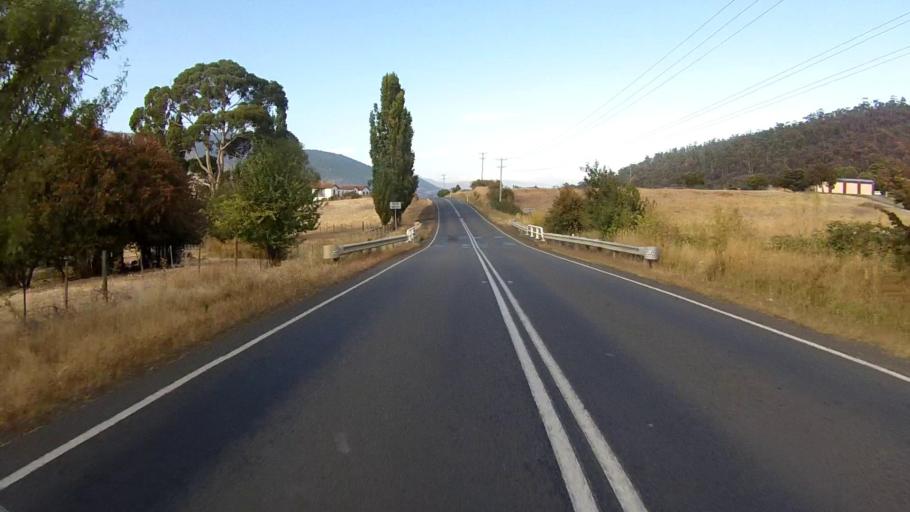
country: AU
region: Tasmania
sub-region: Brighton
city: Bridgewater
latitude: -42.7349
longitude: 147.1750
